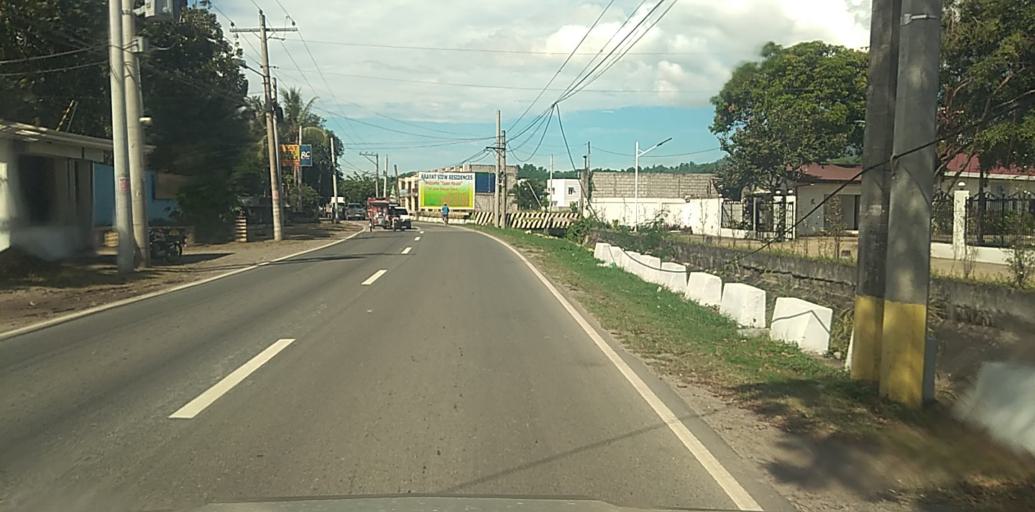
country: PH
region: Central Luzon
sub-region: Province of Pampanga
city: Arayat
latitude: 15.1488
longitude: 120.7577
